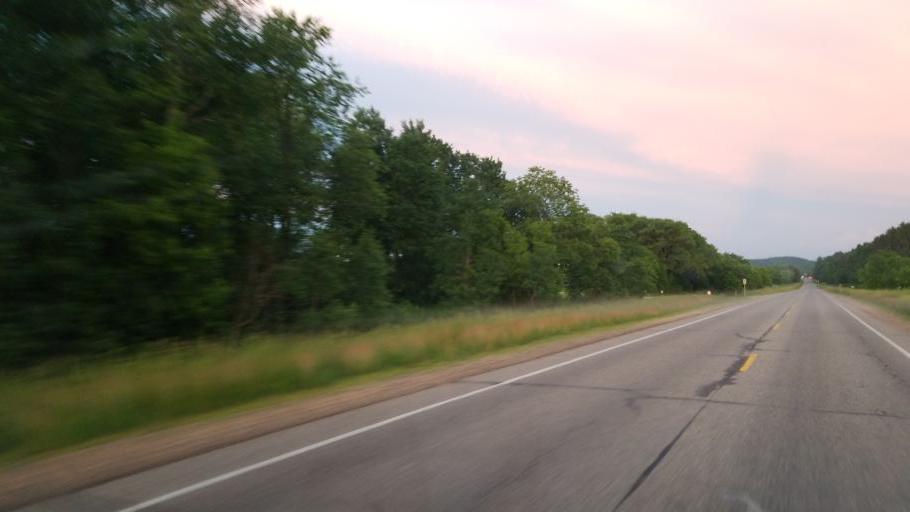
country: US
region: Wisconsin
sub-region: Juneau County
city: Elroy
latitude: 43.7521
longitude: -90.2882
